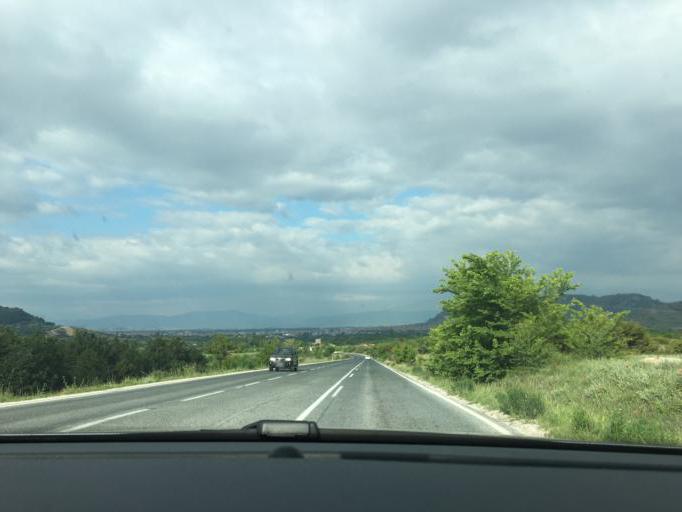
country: MK
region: Prilep
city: Prilep
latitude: 41.3692
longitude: 21.6163
